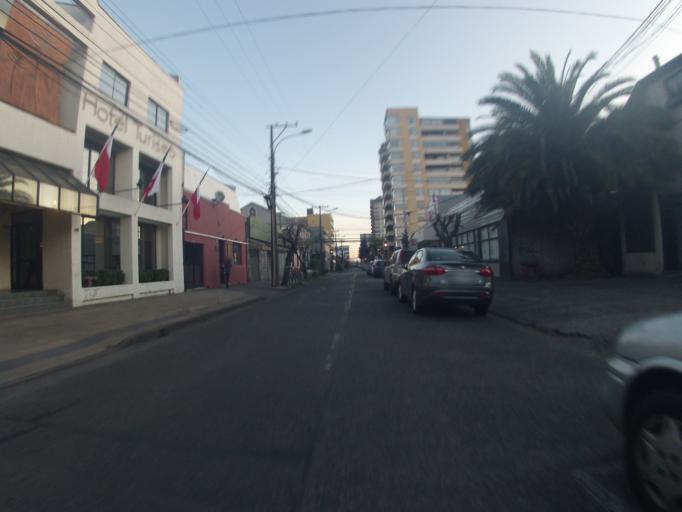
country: CL
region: Araucania
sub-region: Provincia de Cautin
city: Temuco
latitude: -38.7383
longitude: -72.5945
